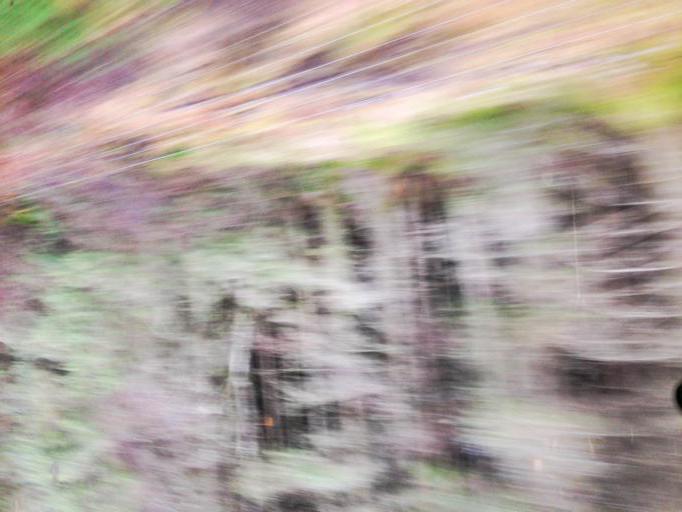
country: GB
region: Scotland
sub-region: Highland
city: Fort William
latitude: 56.8454
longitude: -5.1556
